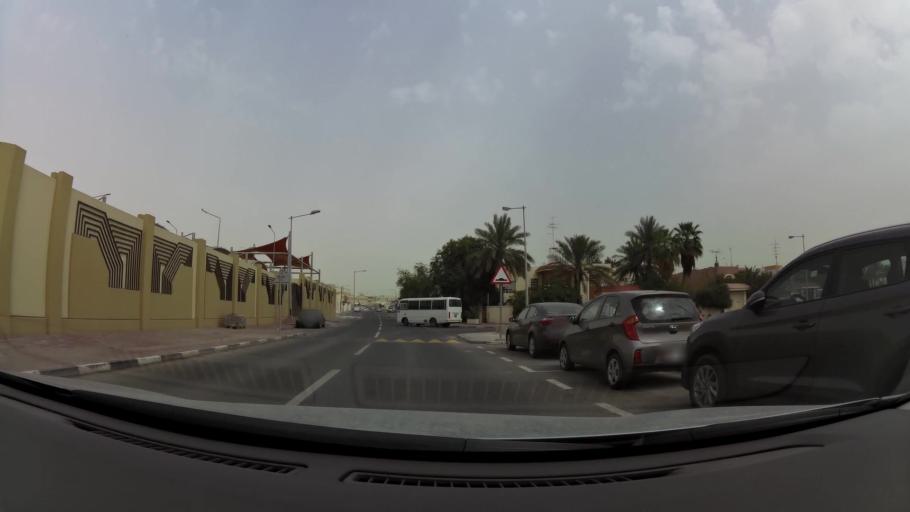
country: QA
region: Baladiyat ad Dawhah
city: Doha
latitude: 25.2565
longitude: 51.5277
